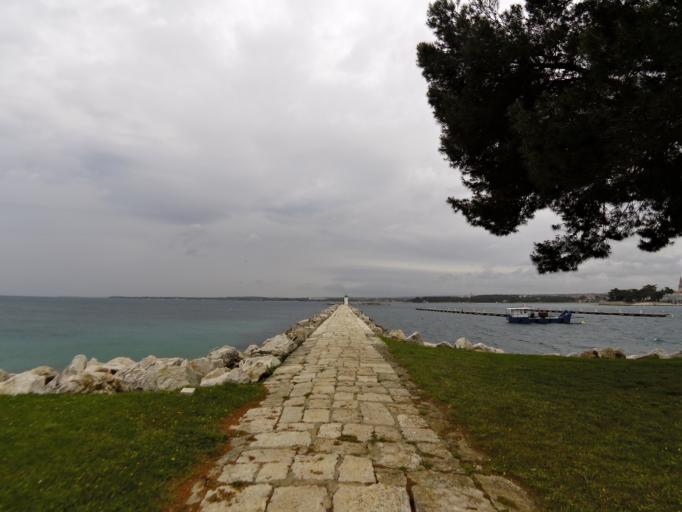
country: HR
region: Istarska
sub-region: Grad Porec
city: Porec
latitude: 45.2264
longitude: 13.5836
